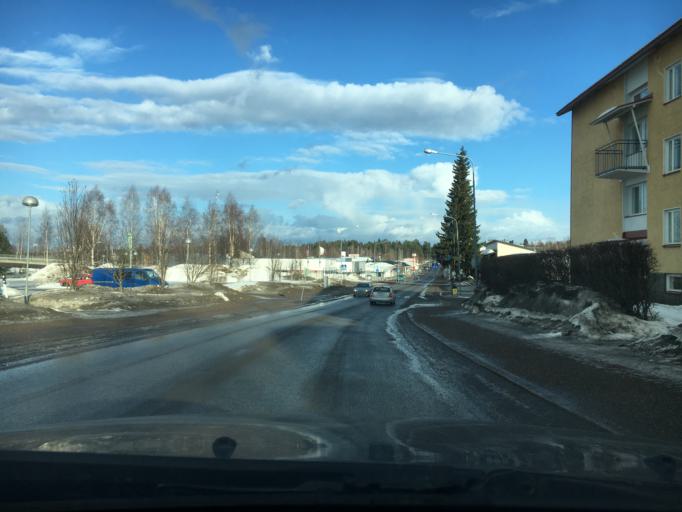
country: FI
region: Kainuu
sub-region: Kajaani
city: Kajaani
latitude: 64.2179
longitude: 27.7327
